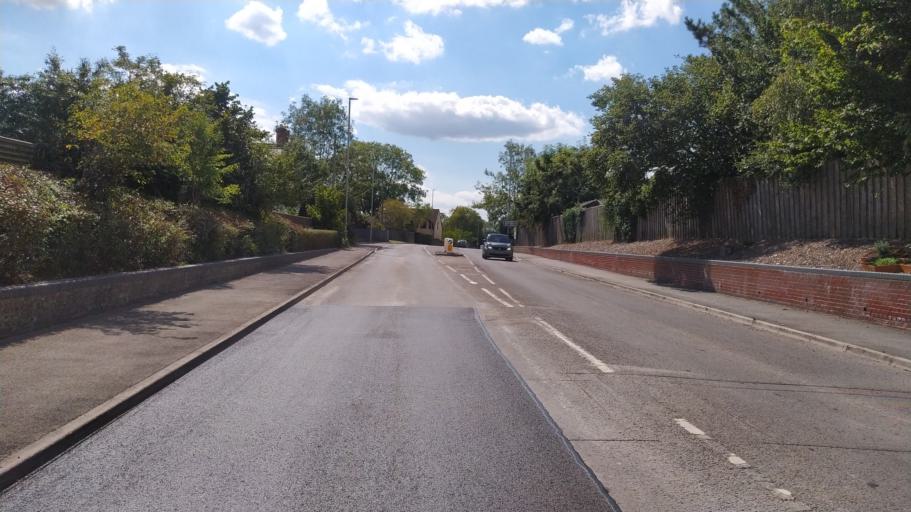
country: GB
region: England
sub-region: Dorset
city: Gillingham
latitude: 51.0401
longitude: -2.2777
